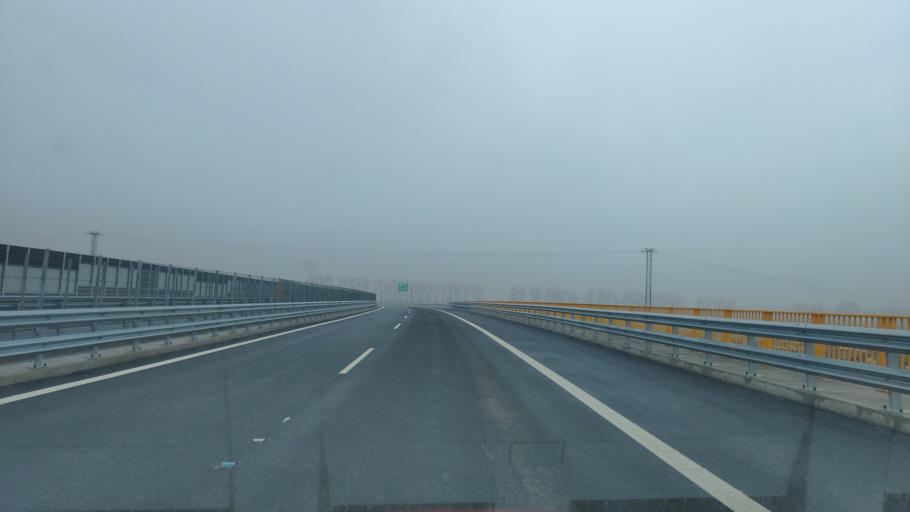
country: SK
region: Kosicky
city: Kosice
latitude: 48.7698
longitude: 21.3249
